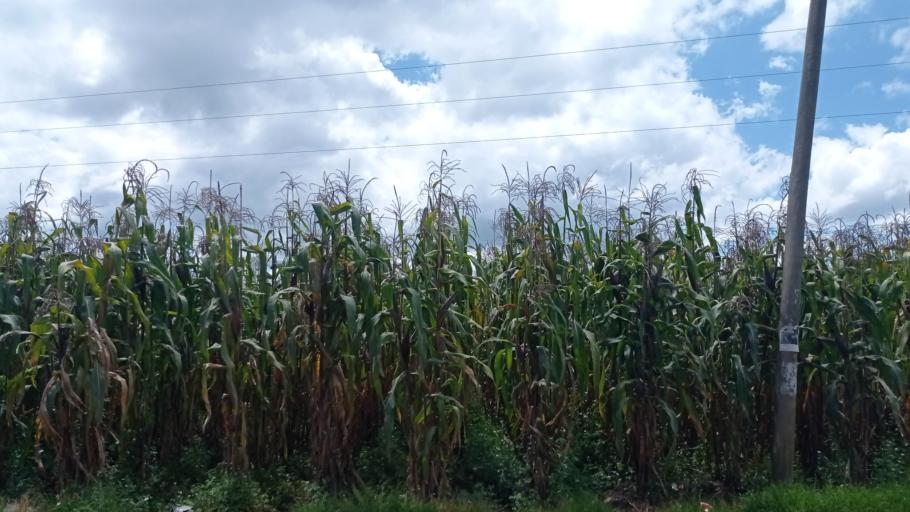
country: GT
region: Quetzaltenango
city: Olintepeque
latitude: 14.8691
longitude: -91.5027
